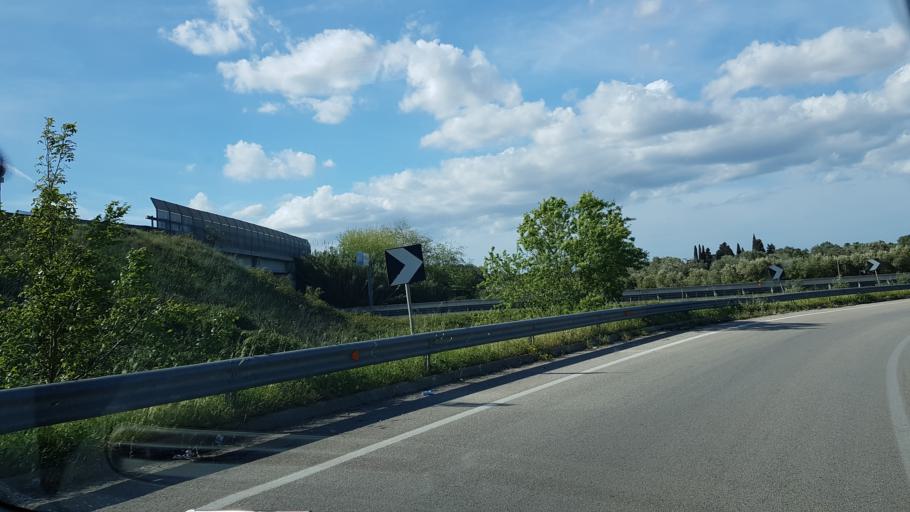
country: IT
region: Apulia
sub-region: Provincia di Brindisi
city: Mesagne
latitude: 40.5671
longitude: 17.7862
